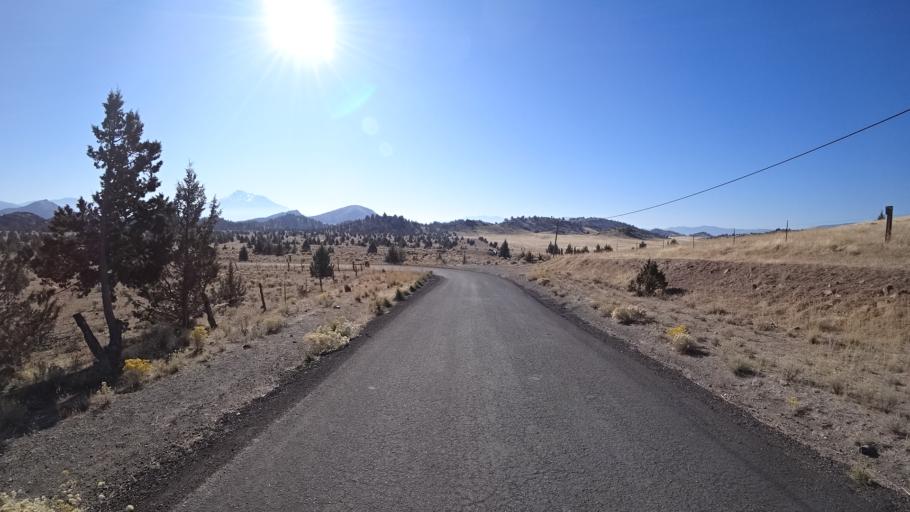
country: US
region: California
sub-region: Siskiyou County
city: Montague
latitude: 41.6970
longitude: -122.4376
